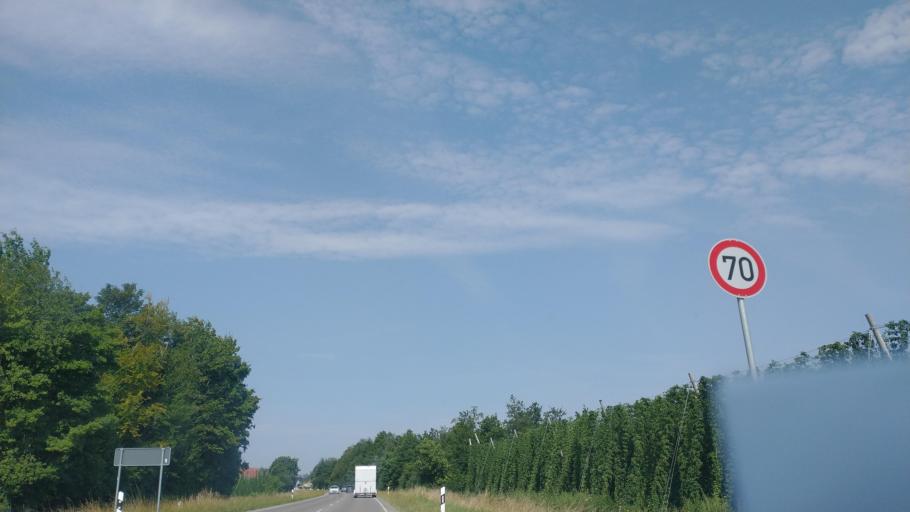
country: DE
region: Baden-Wuerttemberg
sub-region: Tuebingen Region
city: Tettnang
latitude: 47.6659
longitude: 9.5687
